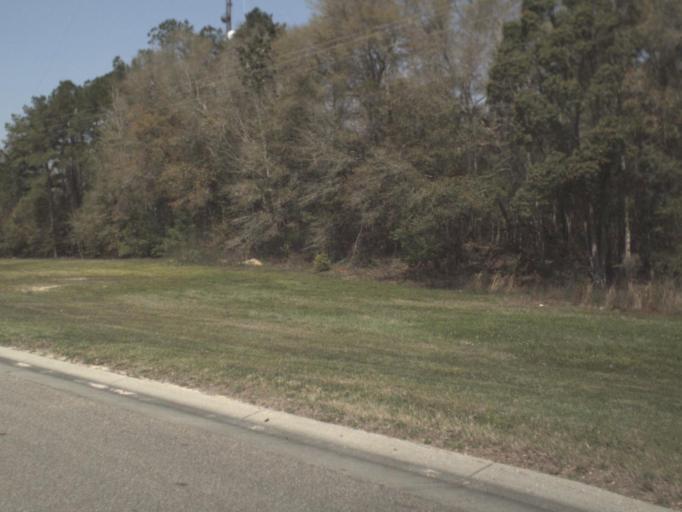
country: US
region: Florida
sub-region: Liberty County
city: Bristol
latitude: 30.4316
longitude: -84.9898
